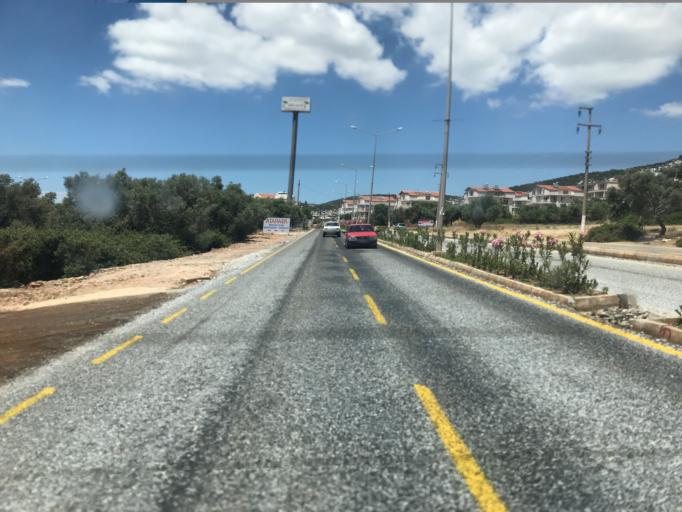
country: TR
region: Aydin
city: Sarikemer
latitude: 37.4162
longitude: 27.4177
